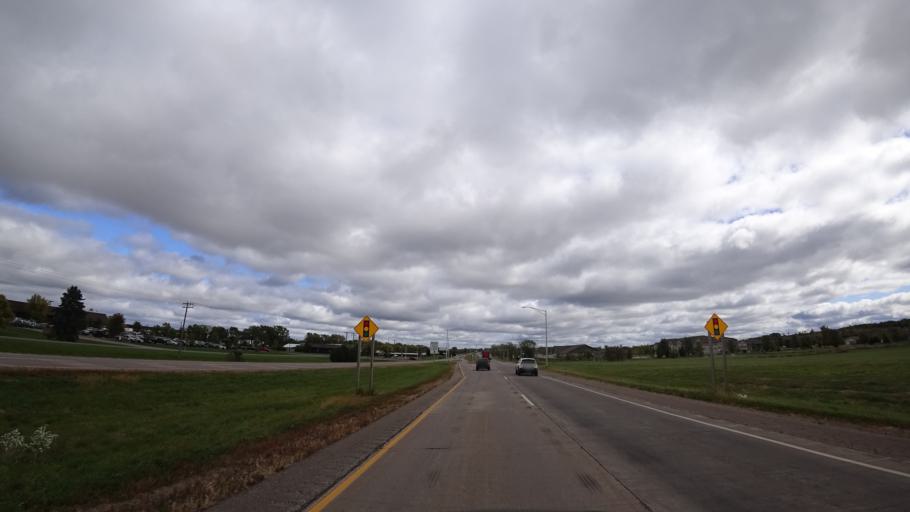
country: US
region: Wisconsin
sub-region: Eau Claire County
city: Eau Claire
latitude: 44.8434
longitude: -91.5840
